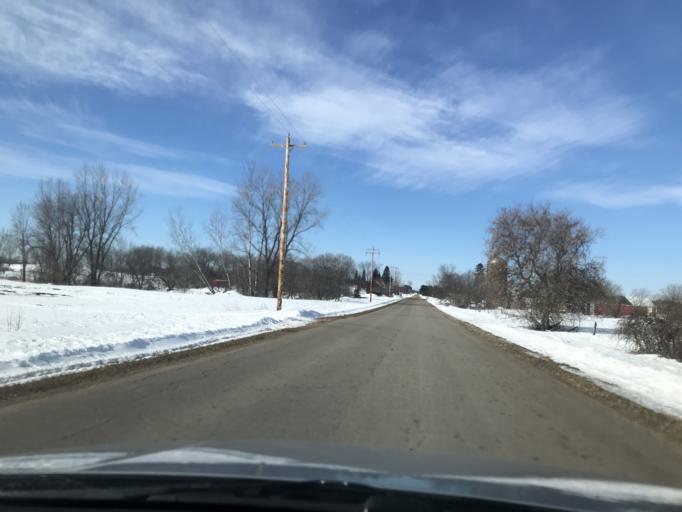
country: US
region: Wisconsin
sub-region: Oconto County
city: Gillett
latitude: 44.9693
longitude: -88.3229
